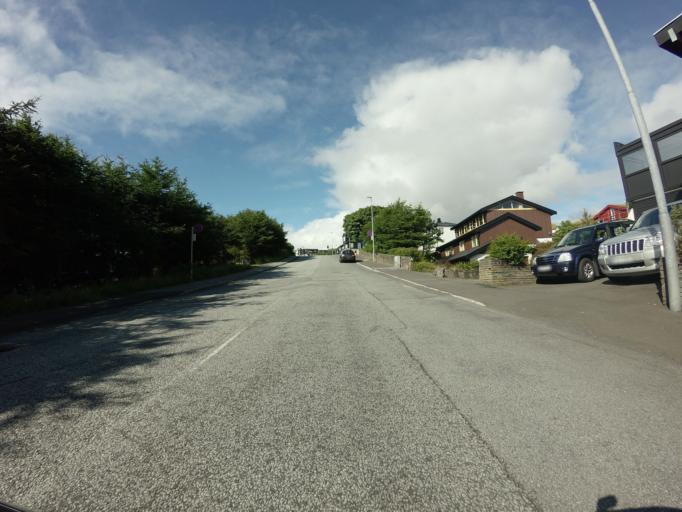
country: FO
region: Streymoy
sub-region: Torshavn
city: Torshavn
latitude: 62.0067
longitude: -6.7861
